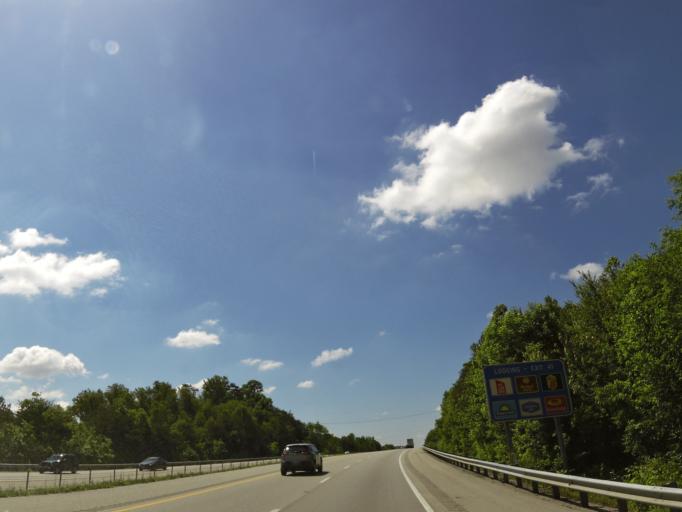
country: US
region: Kentucky
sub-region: Laurel County
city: London
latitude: 37.1595
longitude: -84.1137
